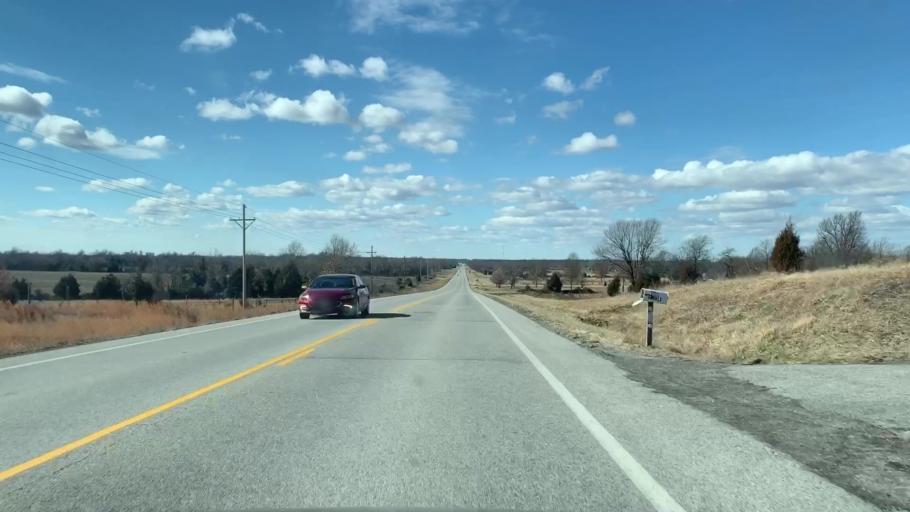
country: US
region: Kansas
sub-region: Cherokee County
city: Columbus
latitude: 37.1781
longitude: -94.7892
